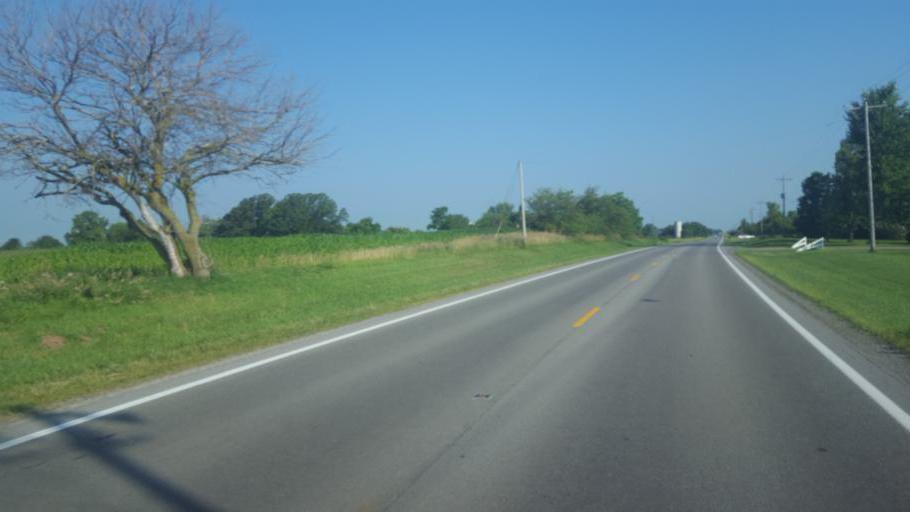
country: US
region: Ohio
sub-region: Hardin County
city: Kenton
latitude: 40.5529
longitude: -83.5364
